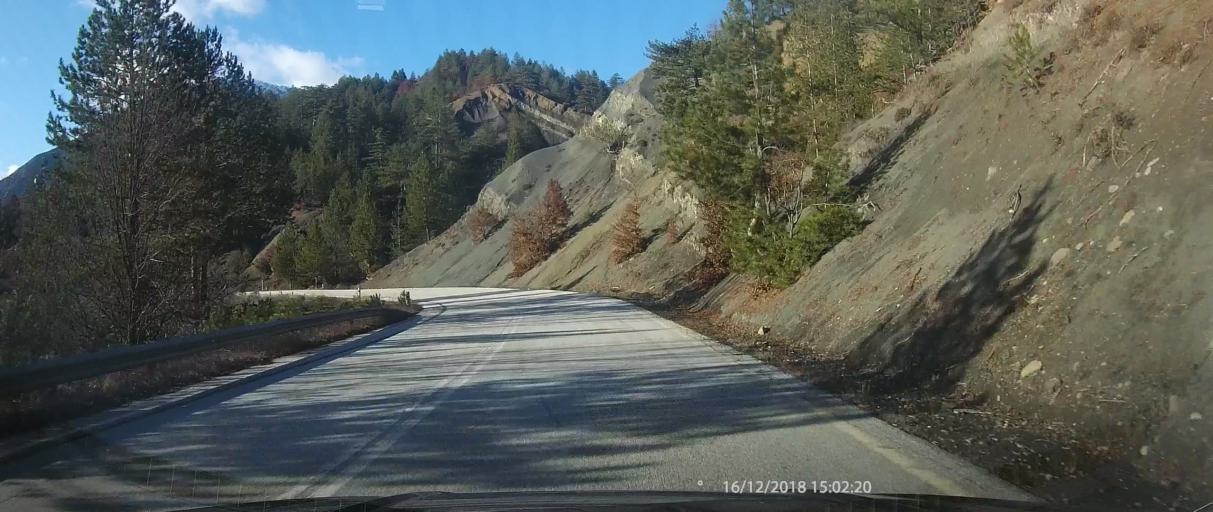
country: GR
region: West Macedonia
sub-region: Nomos Kastorias
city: Nestorio
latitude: 40.2292
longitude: 20.9963
